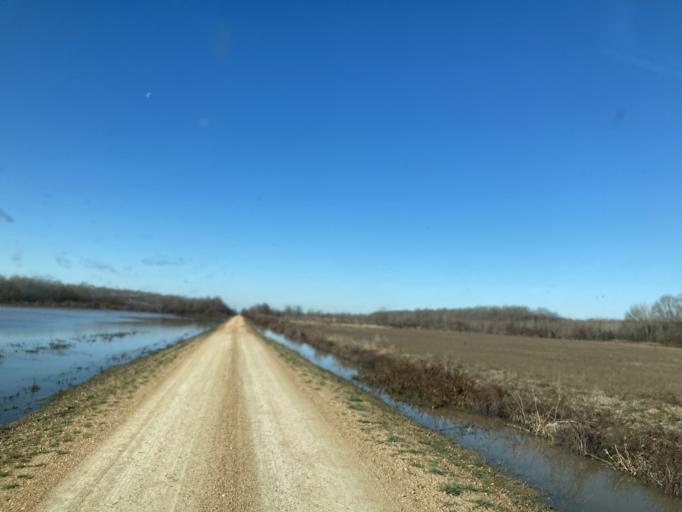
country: US
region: Mississippi
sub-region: Yazoo County
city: Yazoo City
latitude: 32.9518
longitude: -90.6198
